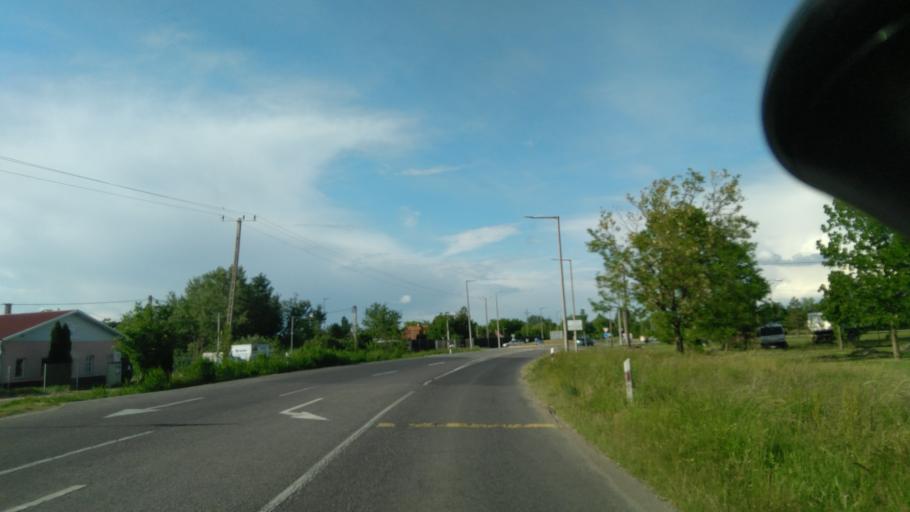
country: HU
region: Bekes
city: Gyula
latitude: 46.6325
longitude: 21.2566
